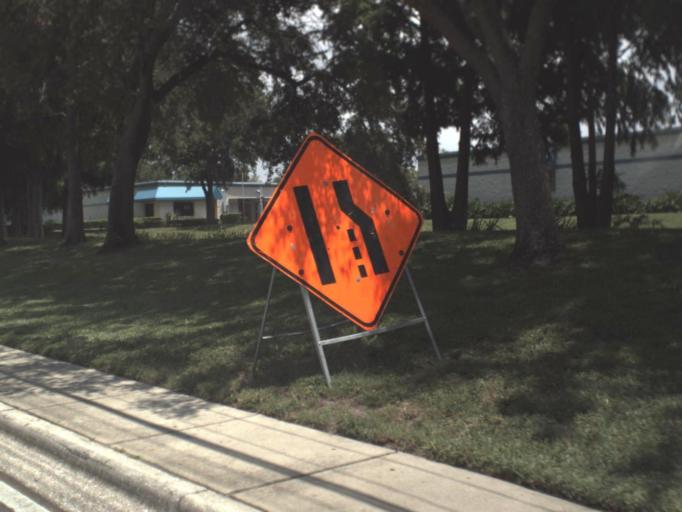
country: US
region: Florida
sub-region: Pinellas County
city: Gulfport
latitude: 27.7284
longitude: -82.6792
